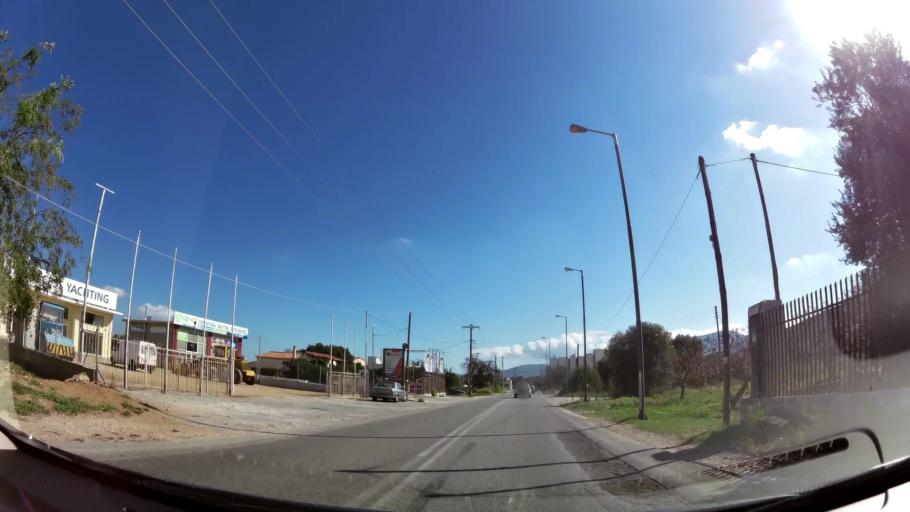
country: GR
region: Attica
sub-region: Nomarchia Anatolikis Attikis
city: Markopoulo
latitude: 37.8870
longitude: 23.9052
